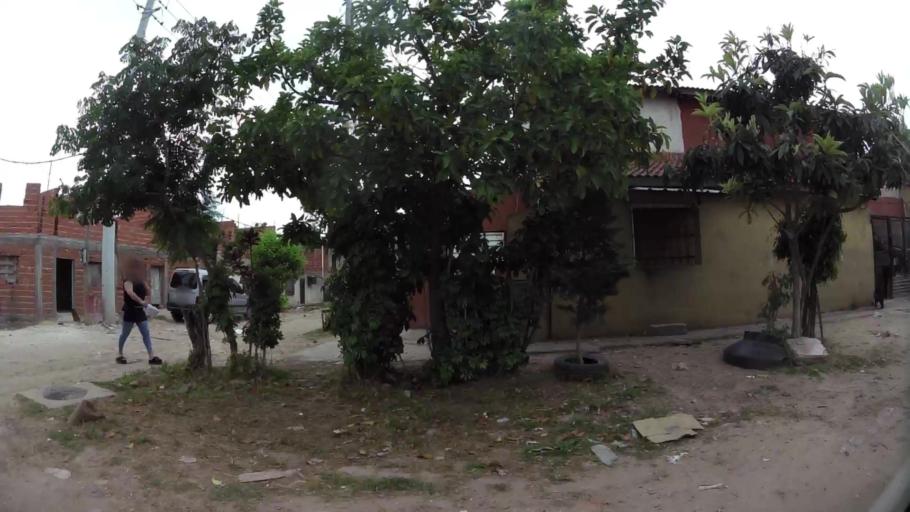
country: AR
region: Buenos Aires
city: San Justo
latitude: -34.6751
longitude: -58.5232
